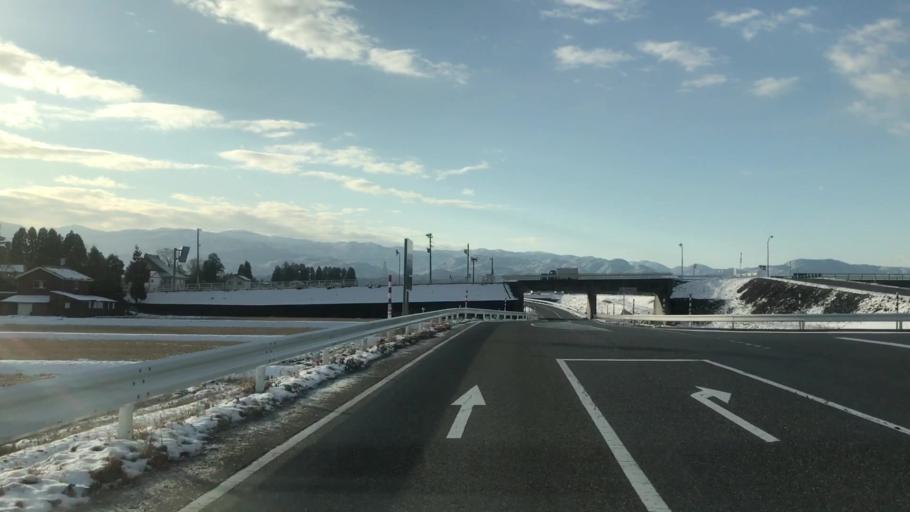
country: JP
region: Toyama
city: Toyama-shi
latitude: 36.6501
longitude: 137.2862
